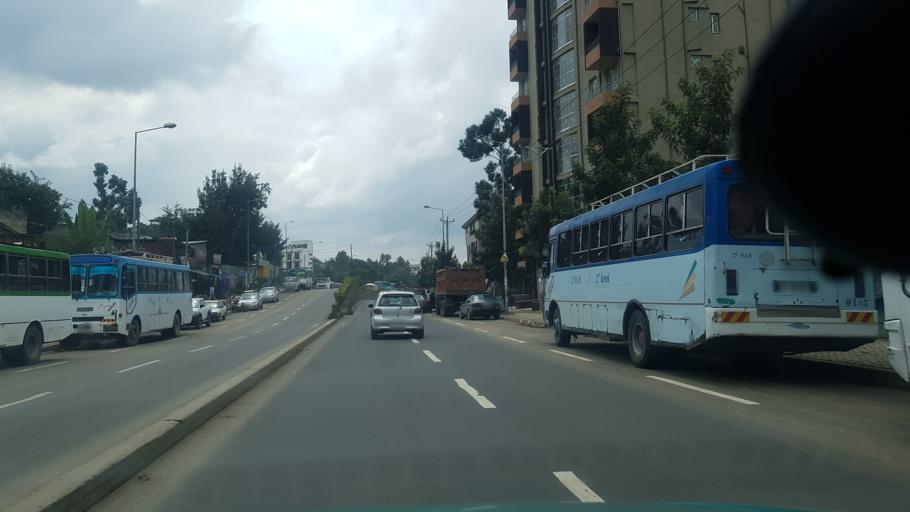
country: ET
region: Adis Abeba
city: Addis Ababa
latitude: 9.0213
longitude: 38.8080
